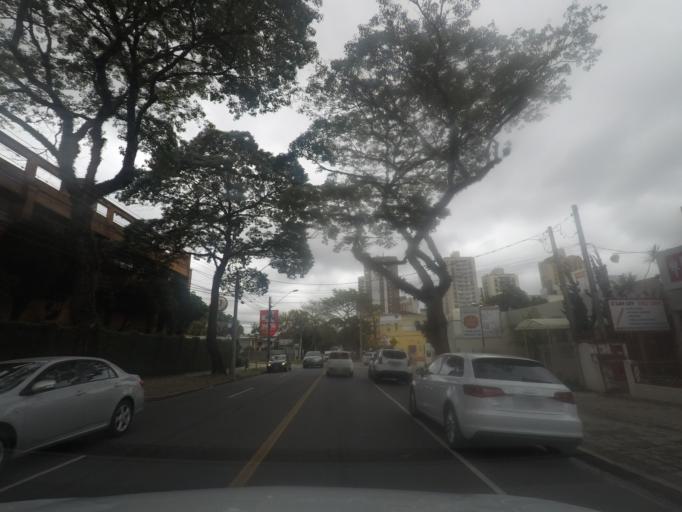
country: BR
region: Parana
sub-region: Curitiba
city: Curitiba
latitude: -25.4321
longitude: -49.2495
